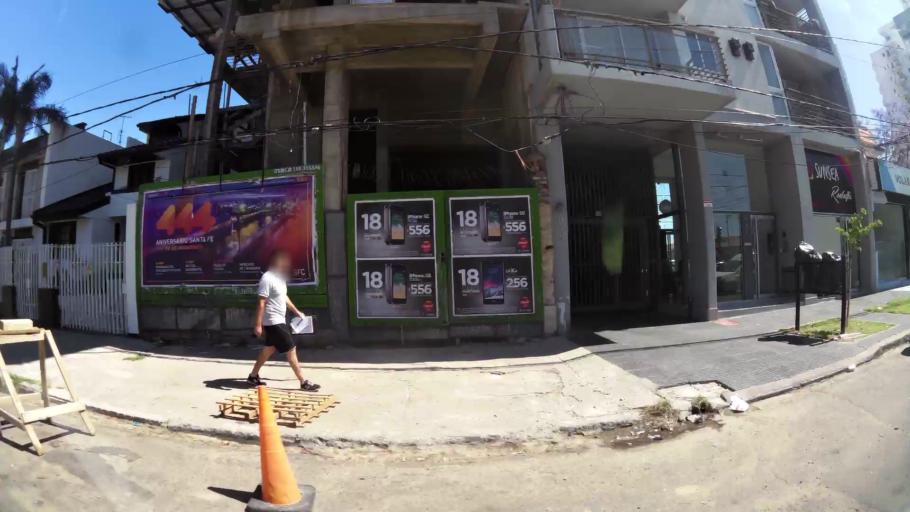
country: AR
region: Santa Fe
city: Santa Fe de la Vera Cruz
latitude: -31.6395
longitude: -60.6857
